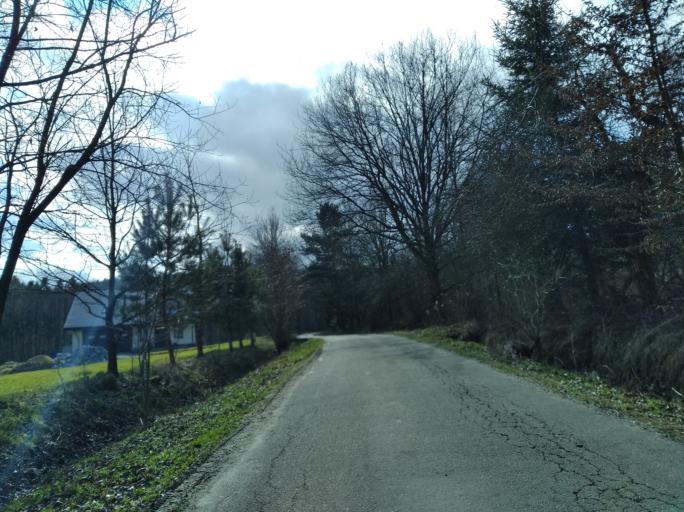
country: PL
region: Subcarpathian Voivodeship
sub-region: Powiat strzyzowski
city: Wysoka Strzyzowska
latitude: 49.8028
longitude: 21.7396
